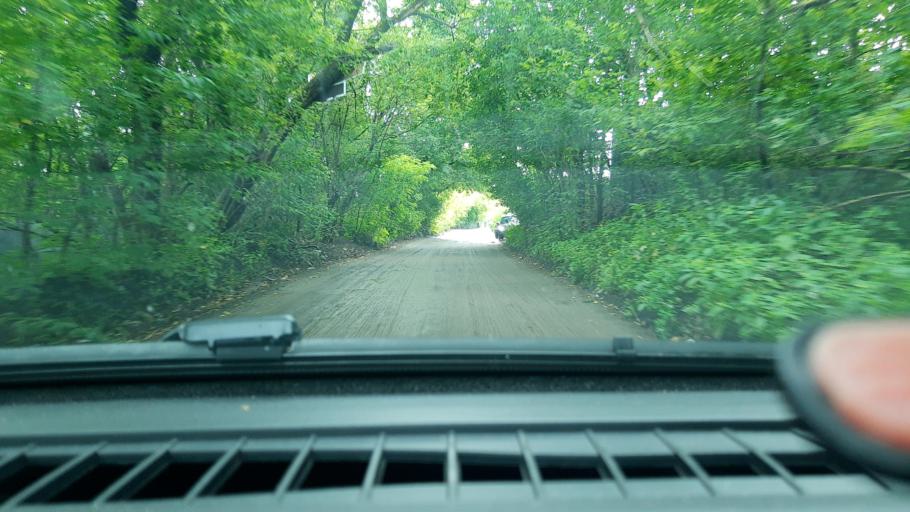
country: RU
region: Nizjnij Novgorod
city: Gorbatovka
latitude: 56.2562
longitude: 43.8309
